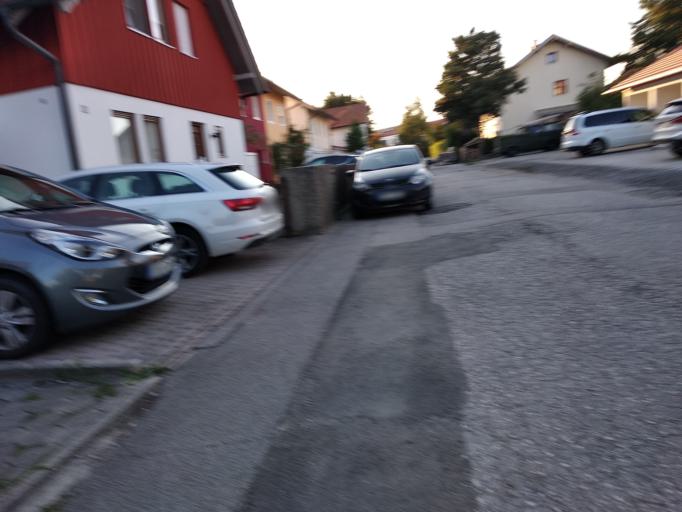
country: DE
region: Bavaria
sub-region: Upper Bavaria
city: Steinhoring
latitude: 48.0888
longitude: 12.0311
